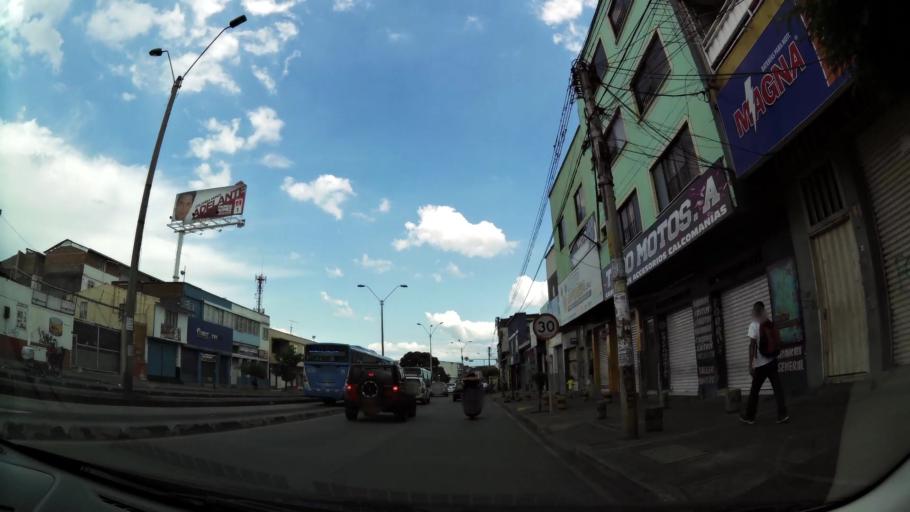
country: CO
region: Valle del Cauca
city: Cali
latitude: 3.4424
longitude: -76.5317
